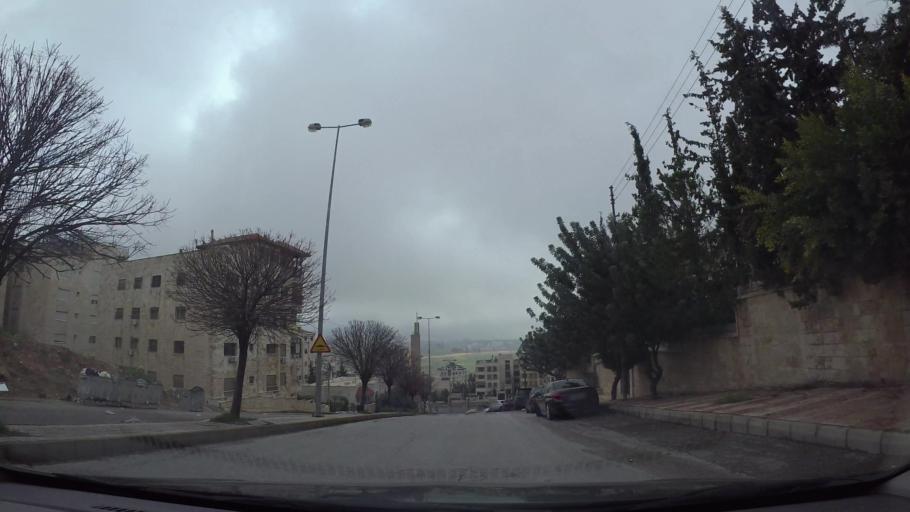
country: JO
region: Amman
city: Wadi as Sir
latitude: 31.9395
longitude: 35.8625
